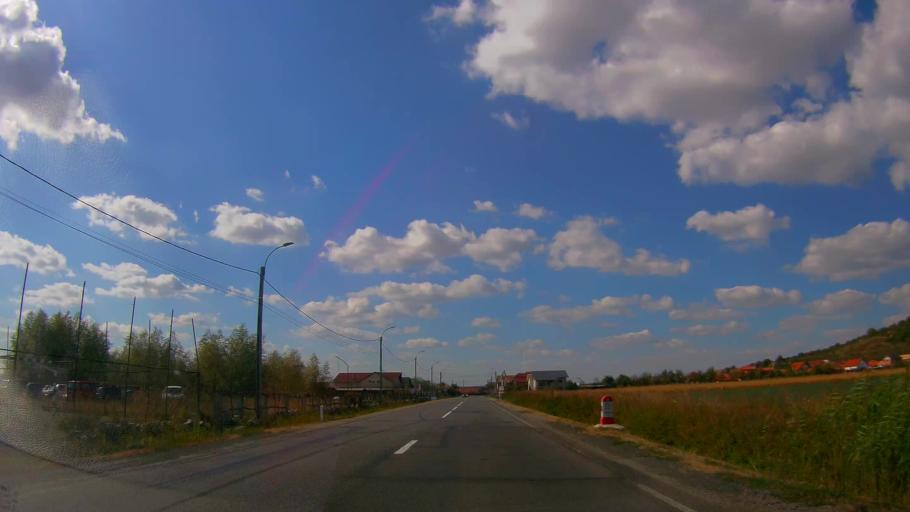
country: RO
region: Salaj
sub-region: Comuna Sarmasag
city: Sarmasag
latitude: 47.3366
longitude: 22.8414
